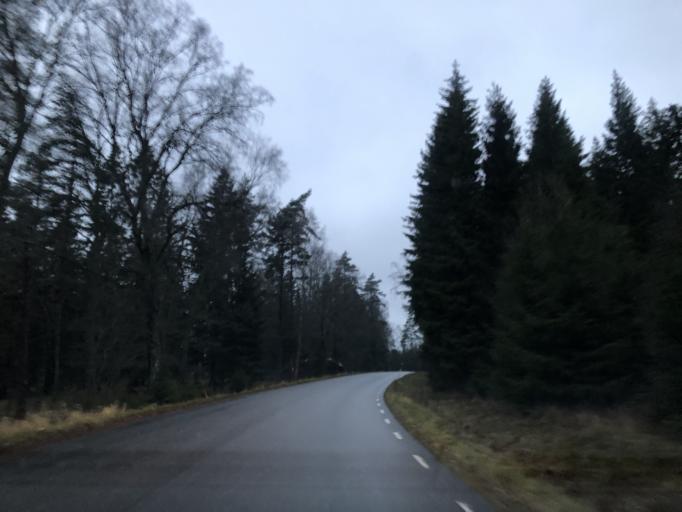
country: SE
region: Vaestra Goetaland
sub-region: Ulricehamns Kommun
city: Ulricehamn
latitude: 57.8503
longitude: 13.2579
